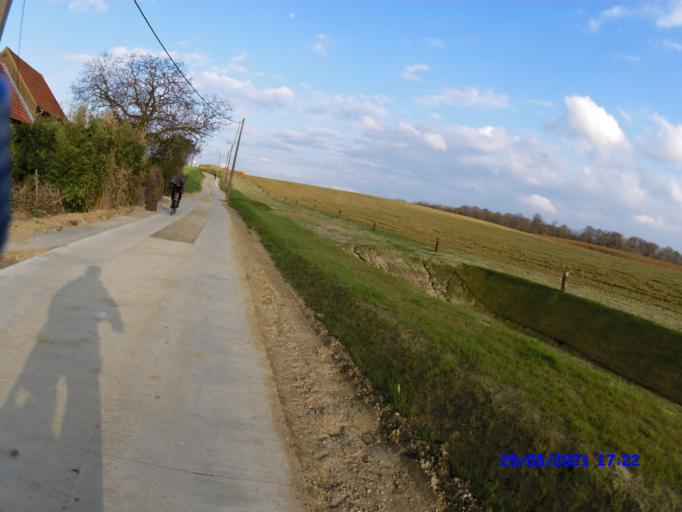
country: BE
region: Flanders
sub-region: Provincie Vlaams-Brabant
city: Wemmel
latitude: 50.8931
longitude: 4.2899
